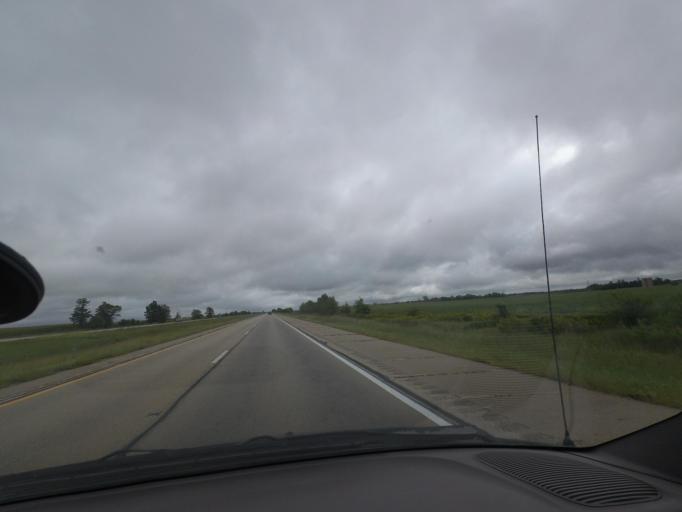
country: US
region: Illinois
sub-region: Piatt County
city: Monticello
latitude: 40.0260
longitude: -88.6721
